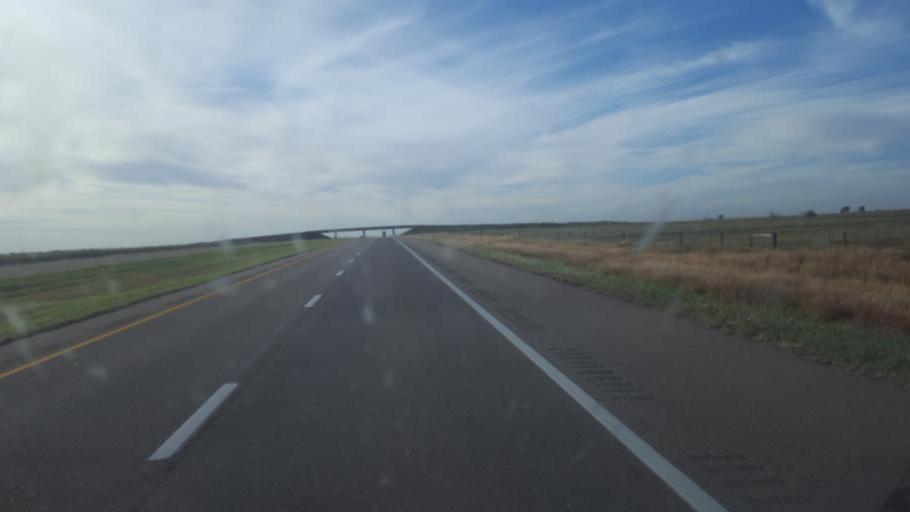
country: US
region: Kansas
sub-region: Gove County
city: Gove
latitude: 39.0736
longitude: -100.2744
